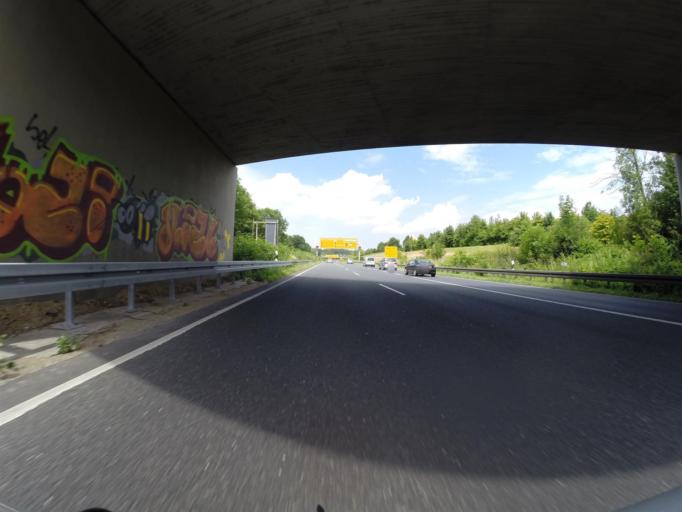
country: DE
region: Lower Saxony
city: Laatzen
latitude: 52.3084
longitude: 9.8236
